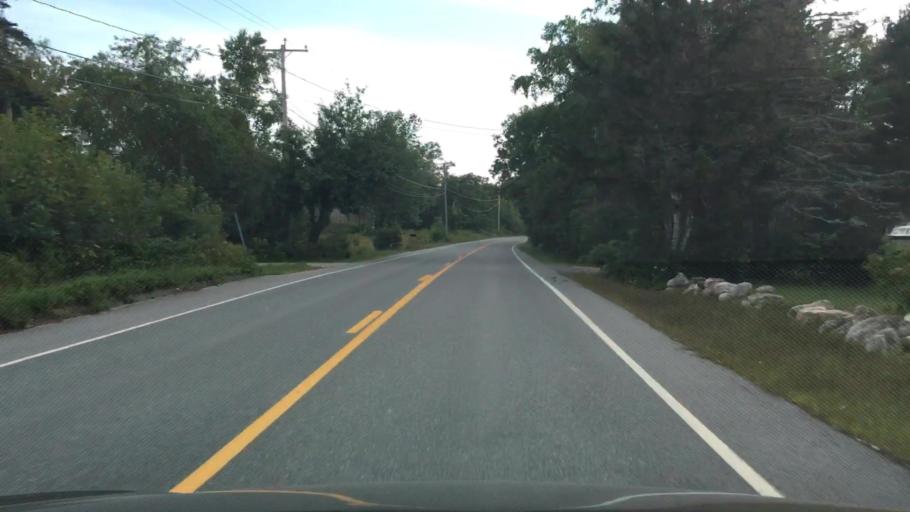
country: US
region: Maine
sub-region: Hancock County
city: Castine
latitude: 44.4379
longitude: -68.7914
